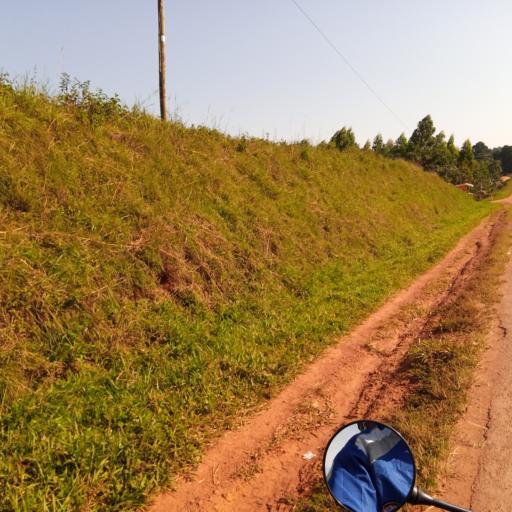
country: UG
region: Central Region
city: Masaka
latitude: -0.4591
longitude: 31.6660
